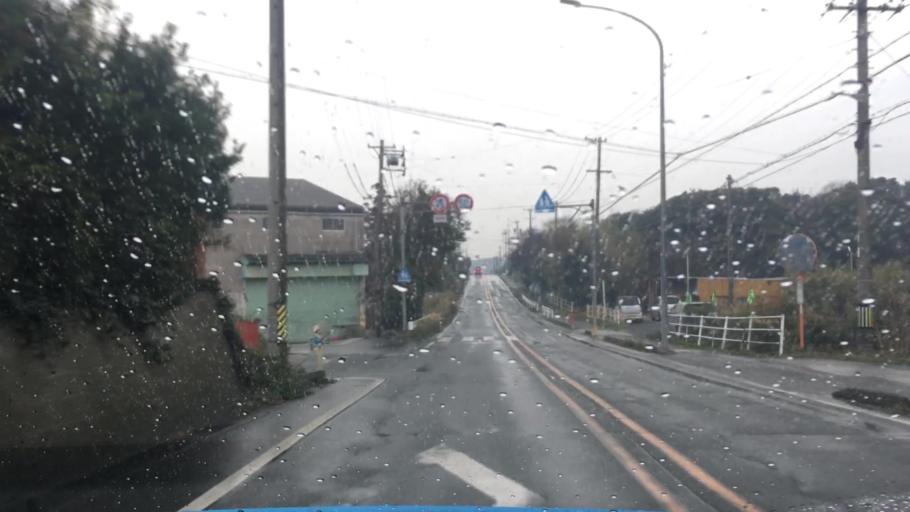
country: JP
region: Aichi
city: Tahara
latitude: 34.6513
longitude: 137.3385
